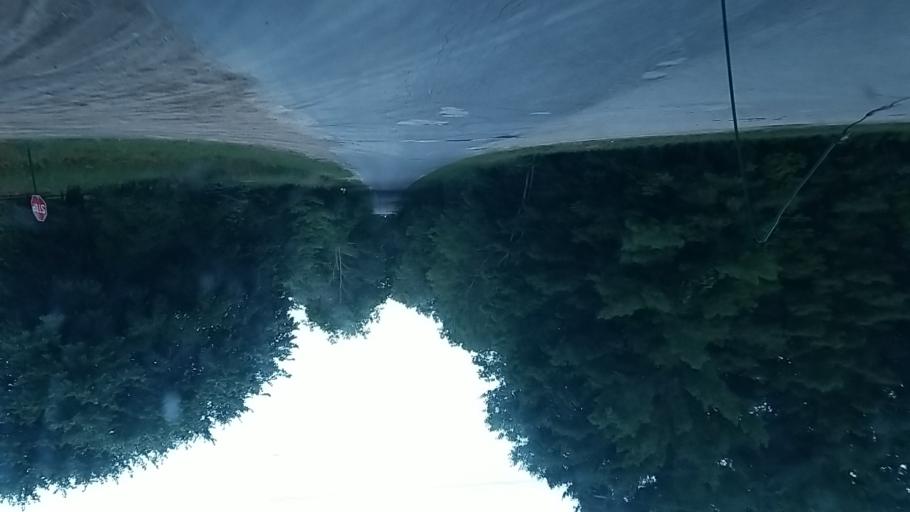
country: US
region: Michigan
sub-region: Newaygo County
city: Fremont
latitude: 43.4820
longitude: -86.0597
